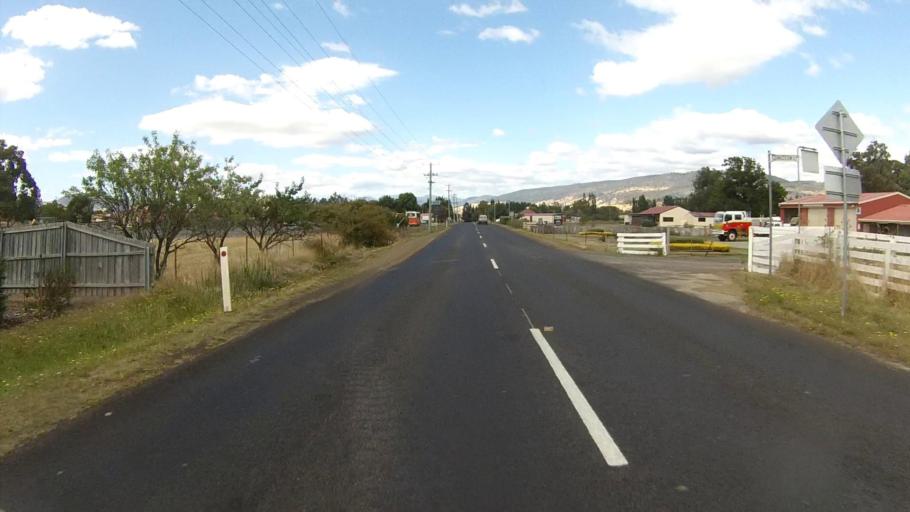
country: AU
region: Tasmania
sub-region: Derwent Valley
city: New Norfolk
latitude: -42.6951
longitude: 146.8876
